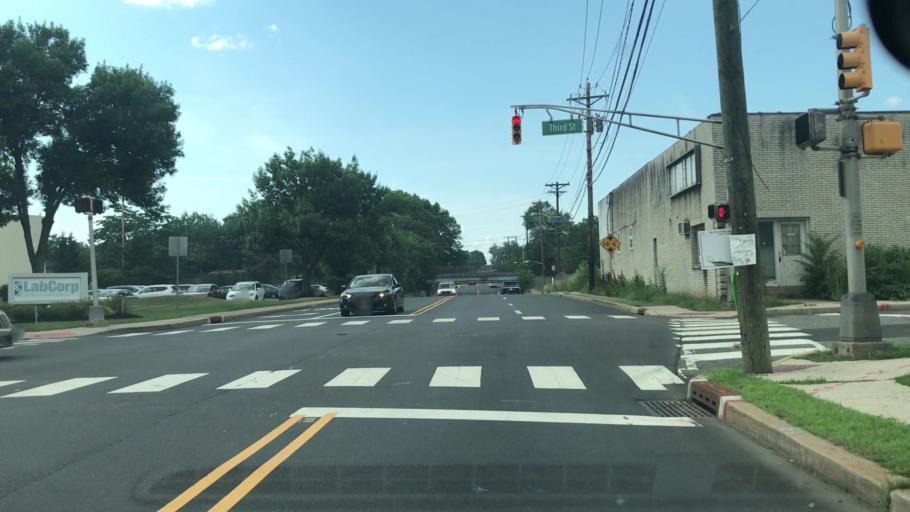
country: US
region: New Jersey
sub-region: Somerset County
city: Raritan
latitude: 40.5695
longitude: -74.6381
